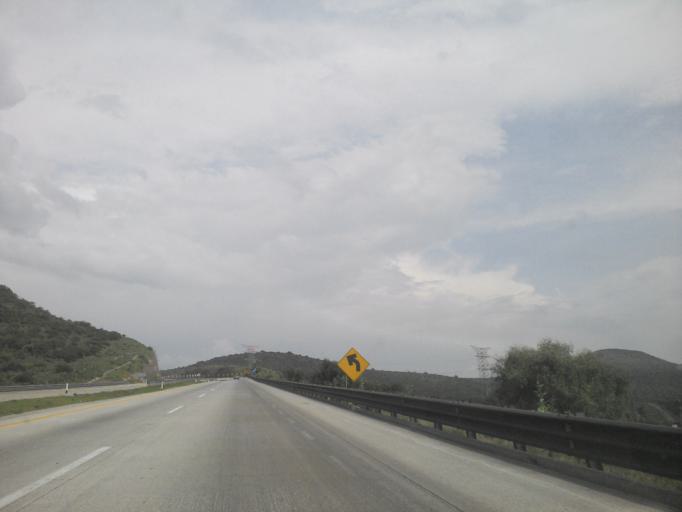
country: MX
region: Mexico
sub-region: Apaxco
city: Colonia Juarez
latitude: 20.0241
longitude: -99.1694
